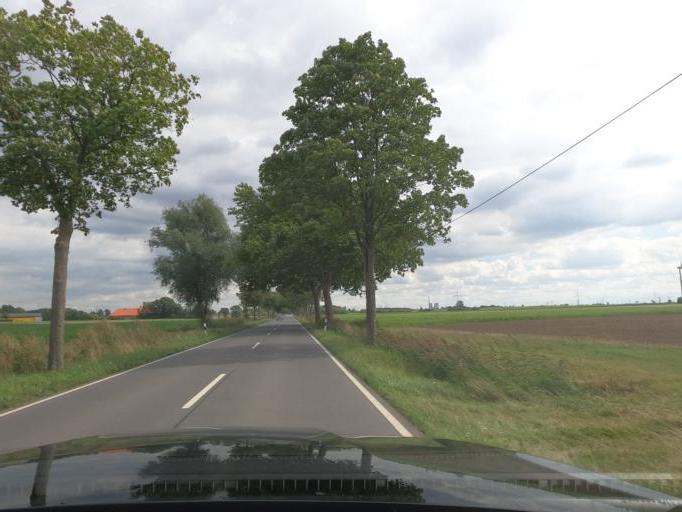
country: DE
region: Lower Saxony
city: Lehrte
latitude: 52.3617
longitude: 10.0048
